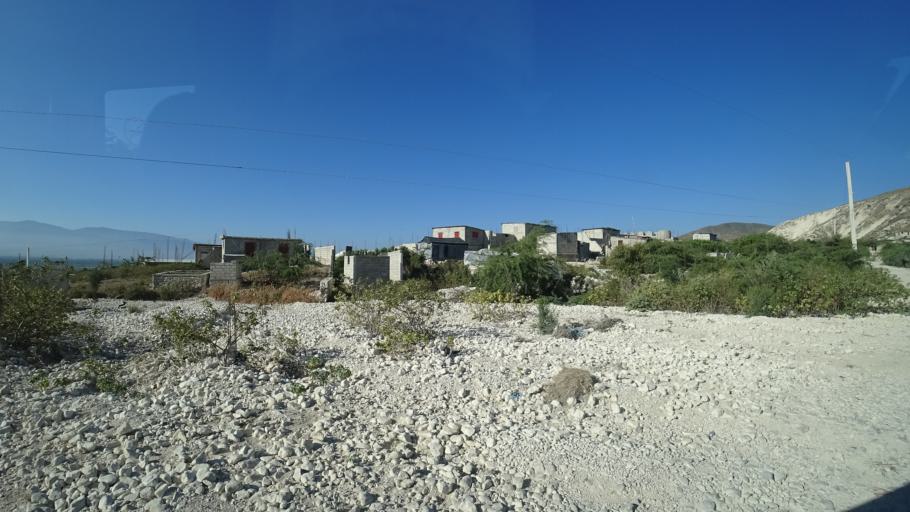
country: HT
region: Ouest
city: Croix des Bouquets
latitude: 18.6719
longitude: -72.2409
